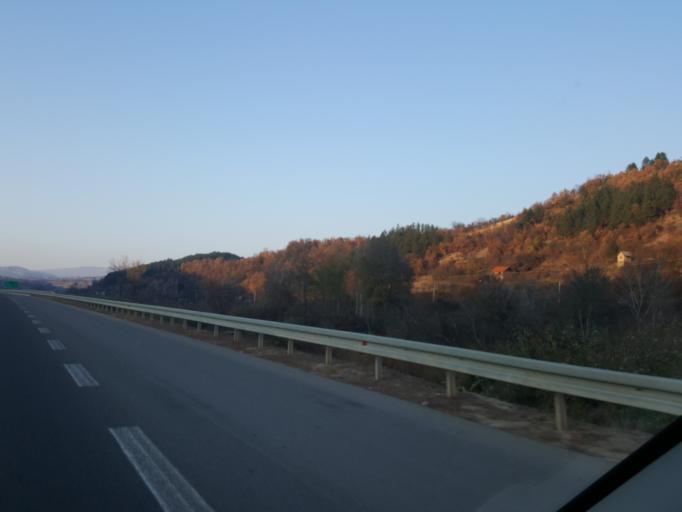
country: RS
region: Central Serbia
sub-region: Pirotski Okrug
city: Pirot
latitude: 43.1918
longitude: 22.5637
